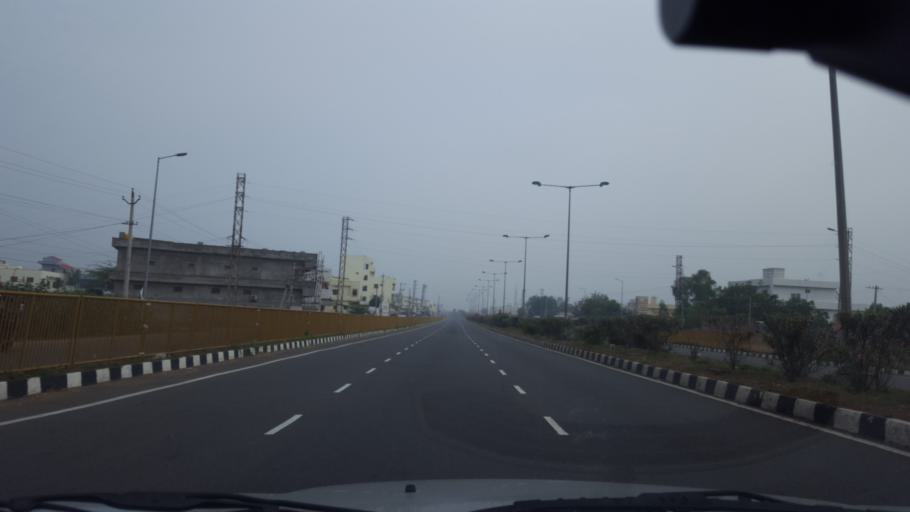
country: IN
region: Andhra Pradesh
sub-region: Prakasam
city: pedda nakkalapalem
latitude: 15.9769
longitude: 80.0991
